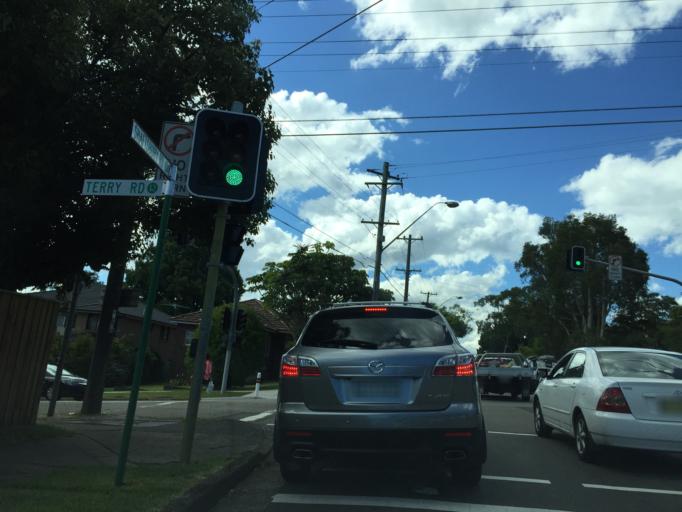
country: AU
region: New South Wales
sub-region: Ryde
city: West Ryde
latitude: -33.7887
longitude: 151.0756
